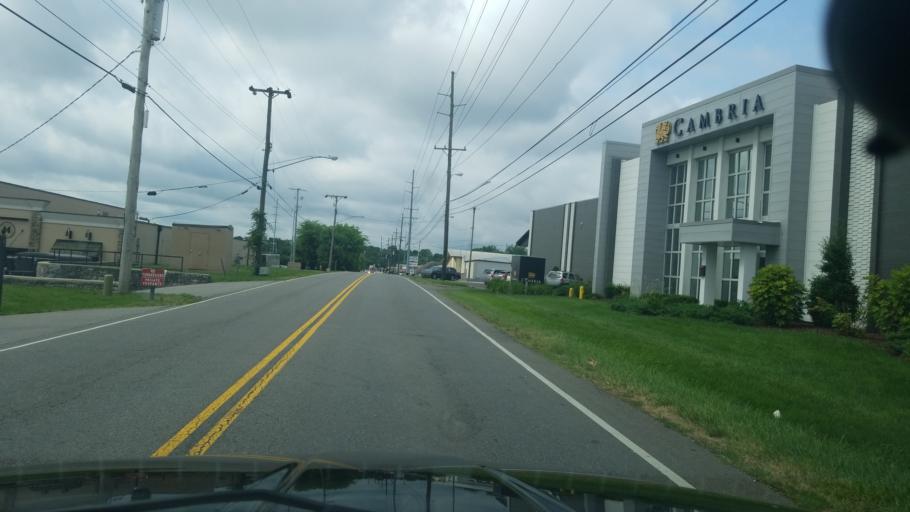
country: US
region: Tennessee
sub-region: Davidson County
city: Oak Hill
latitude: 36.0949
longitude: -86.7496
